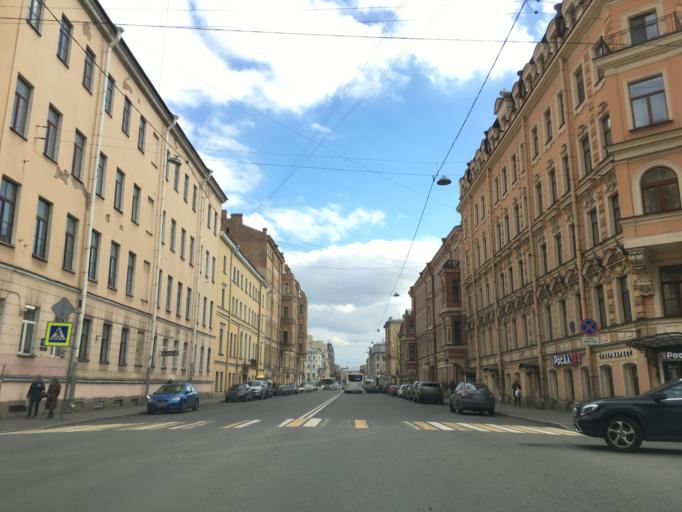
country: RU
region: St.-Petersburg
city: Admiralteisky
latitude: 59.9224
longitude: 30.2856
